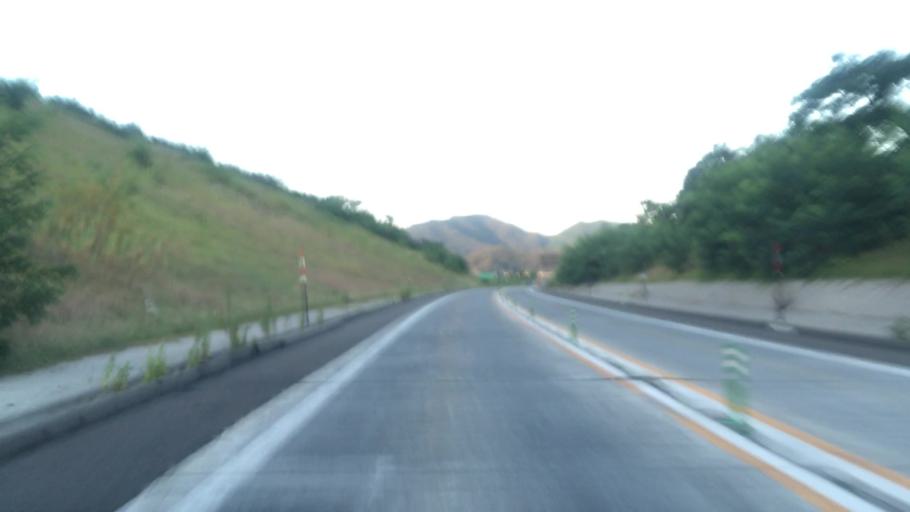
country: JP
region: Tottori
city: Tottori
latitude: 35.5485
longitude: 134.2655
